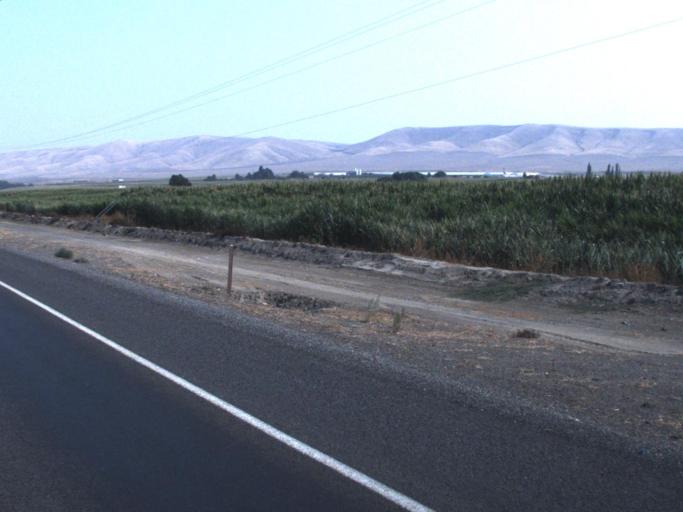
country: US
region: Washington
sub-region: Yakima County
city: Mabton
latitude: 46.1991
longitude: -119.9483
